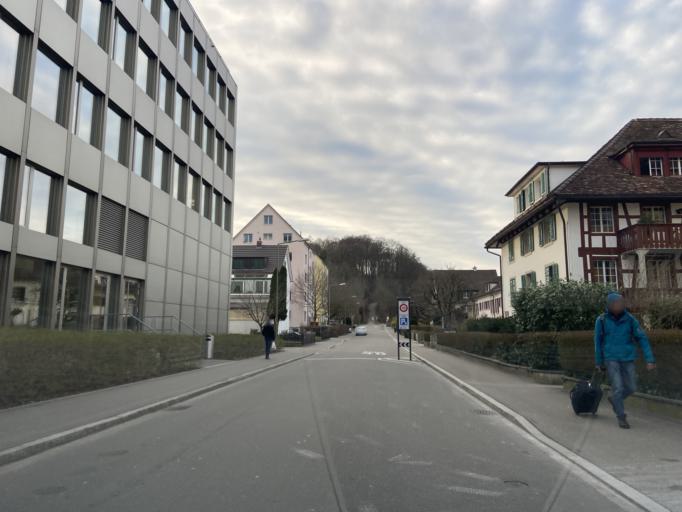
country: CH
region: Zurich
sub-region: Bezirk Winterthur
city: Stadt Winterthur (Kreis 1) / Neuwiesen
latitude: 47.4983
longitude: 8.7169
